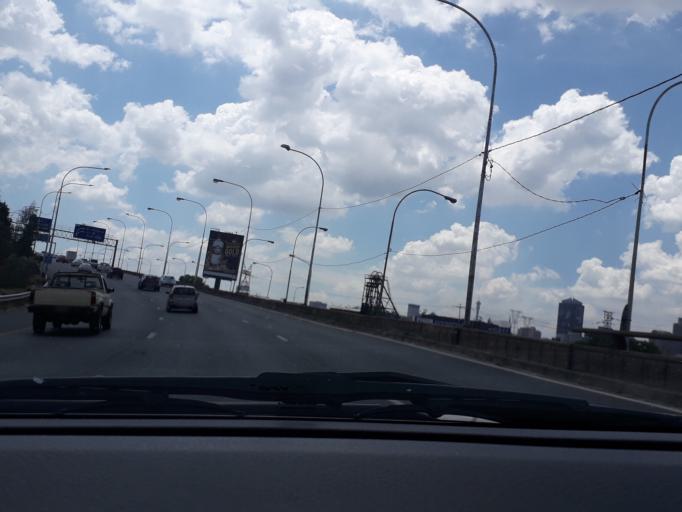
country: ZA
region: Gauteng
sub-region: City of Johannesburg Metropolitan Municipality
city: Johannesburg
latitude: -26.2186
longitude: 28.0232
